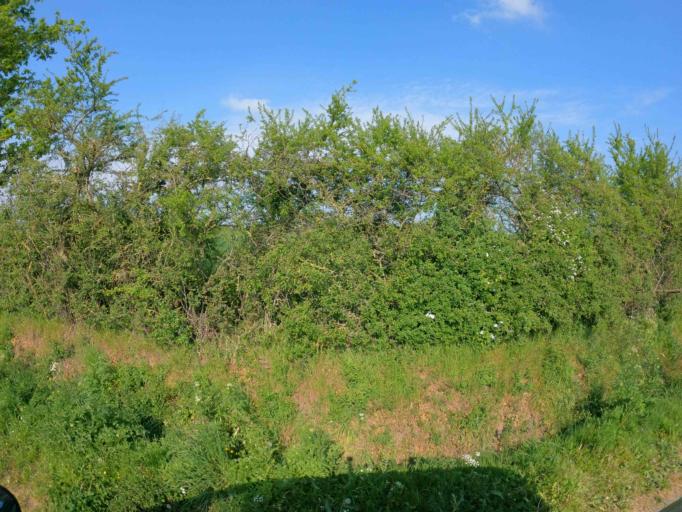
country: FR
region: Pays de la Loire
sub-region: Departement de la Vendee
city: Treize-Septiers
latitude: 47.0015
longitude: -1.2566
